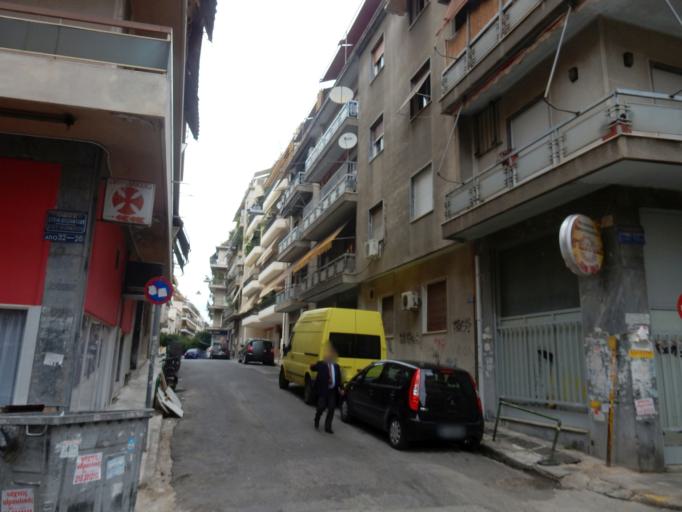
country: GR
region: Attica
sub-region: Nomarchia Athinas
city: Nea Chalkidona
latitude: 38.0154
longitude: 23.7328
